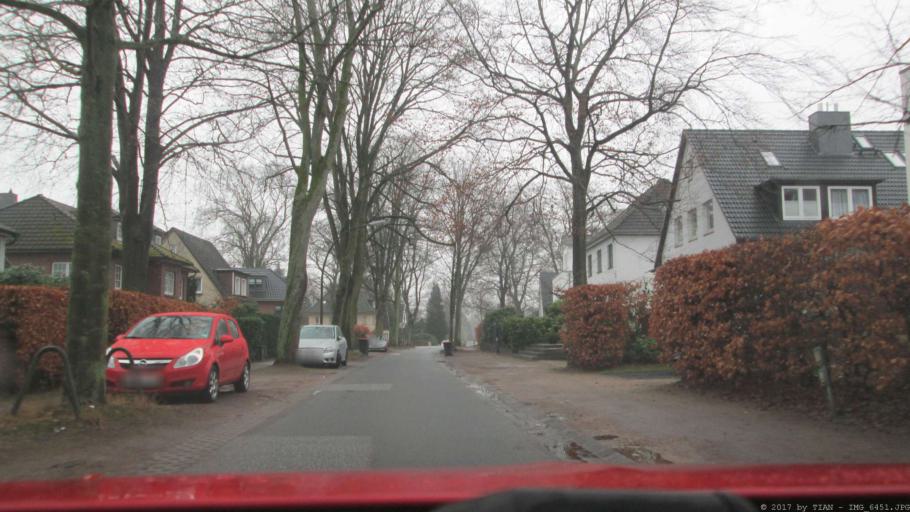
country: DE
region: Schleswig-Holstein
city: Halstenbek
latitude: 53.5728
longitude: 9.8044
